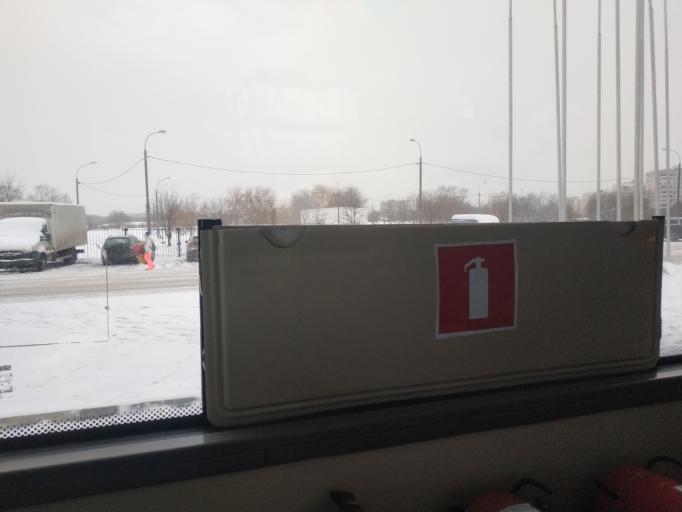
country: RU
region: Moscow
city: Kolomenskoye
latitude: 55.6753
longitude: 37.6785
